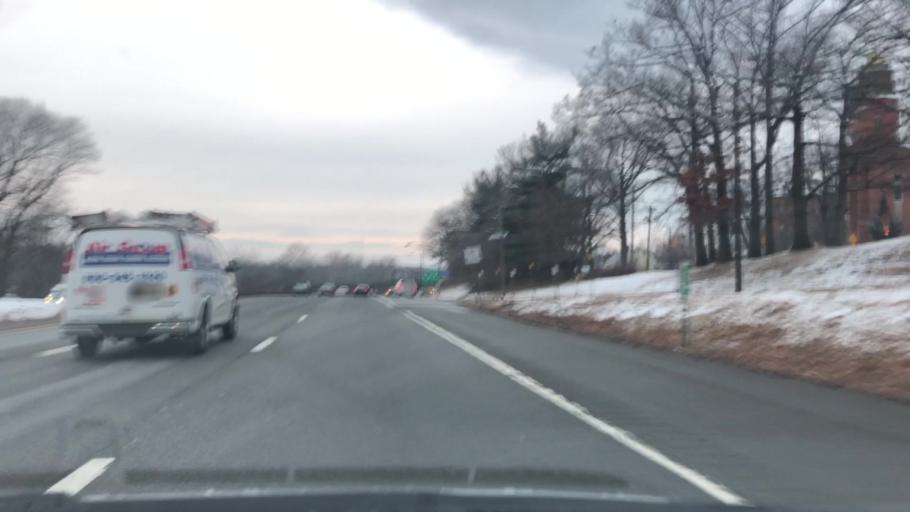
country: US
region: New Jersey
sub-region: Essex County
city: Brookdale
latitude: 40.8303
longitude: -74.1775
